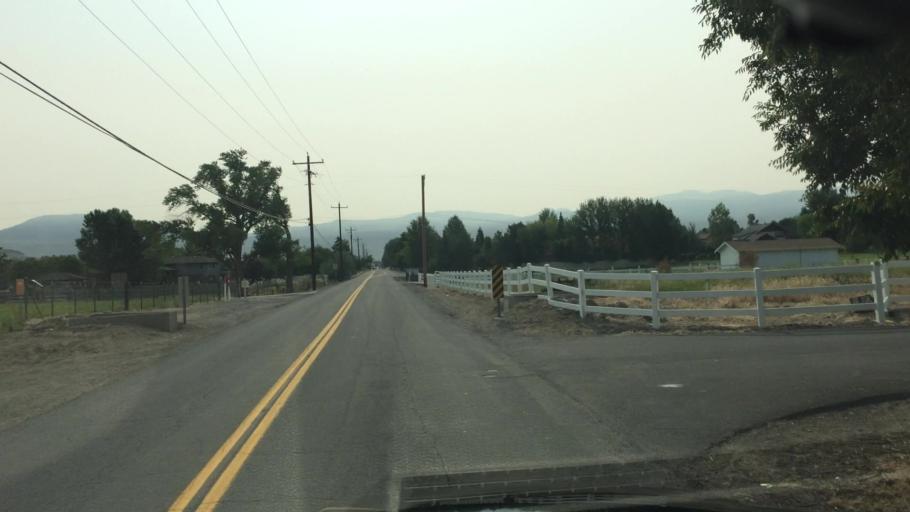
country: US
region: Nevada
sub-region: Washoe County
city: Reno
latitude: 39.4438
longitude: -119.7866
